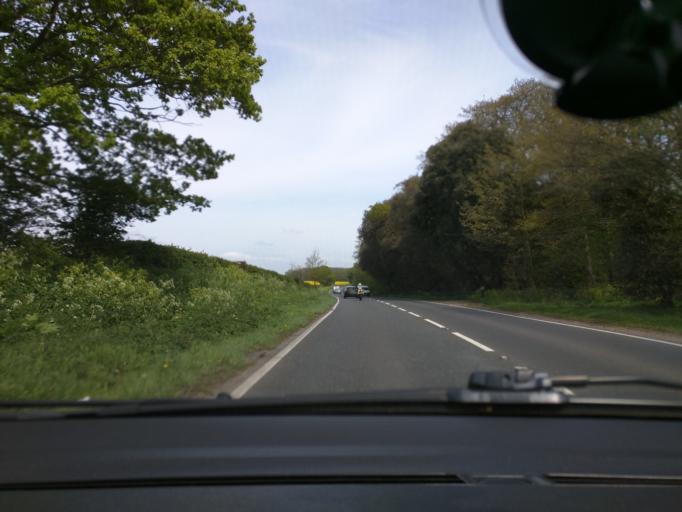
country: GB
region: England
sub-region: Suffolk
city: Wrentham
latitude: 52.3928
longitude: 1.6716
